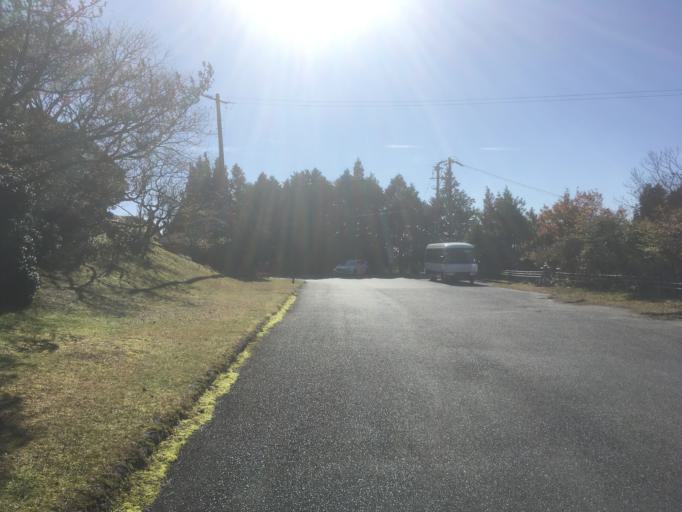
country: JP
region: Mie
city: Ueno-ebisumachi
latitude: 34.6890
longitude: 136.2756
